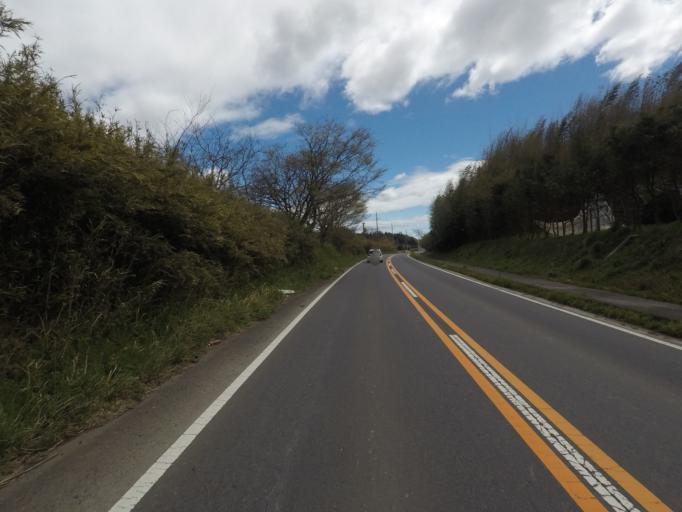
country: JP
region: Ibaraki
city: Itako
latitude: 36.1017
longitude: 140.4892
